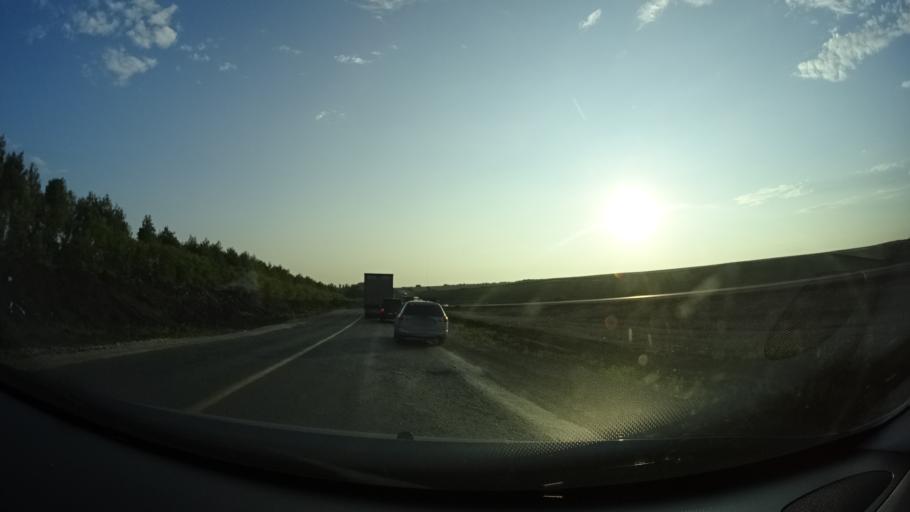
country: RU
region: Samara
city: Kamyshla
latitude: 54.0350
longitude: 51.9420
